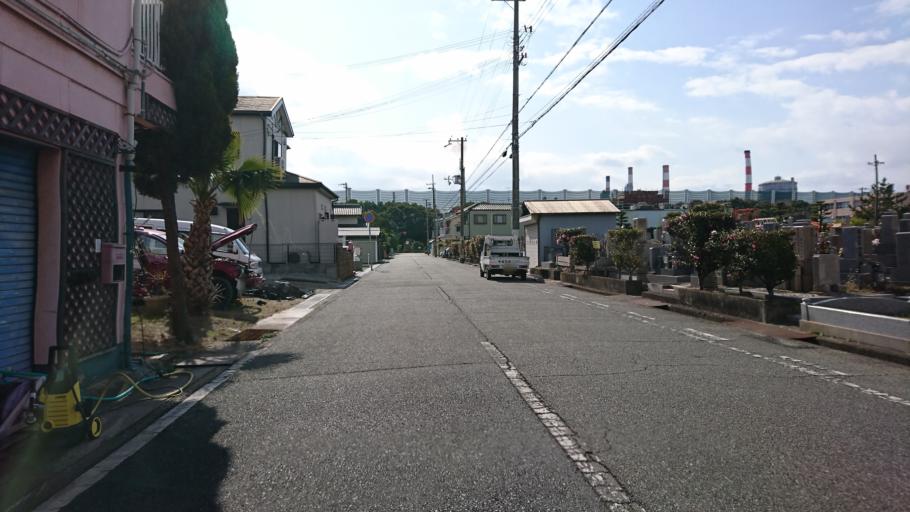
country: JP
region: Hyogo
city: Kakogawacho-honmachi
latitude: 34.7258
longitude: 134.8424
